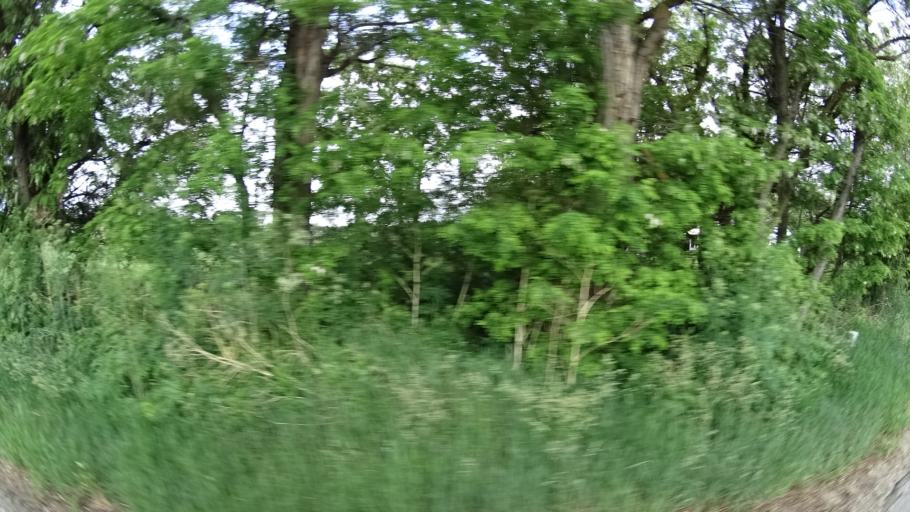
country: US
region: Idaho
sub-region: Ada County
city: Star
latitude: 43.7191
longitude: -116.5127
